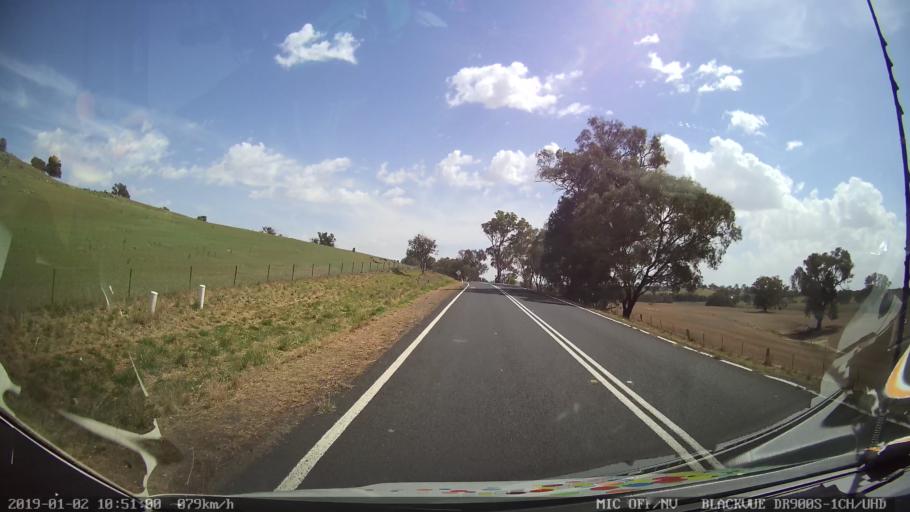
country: AU
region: New South Wales
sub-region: Cootamundra
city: Cootamundra
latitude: -34.7060
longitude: 148.2756
